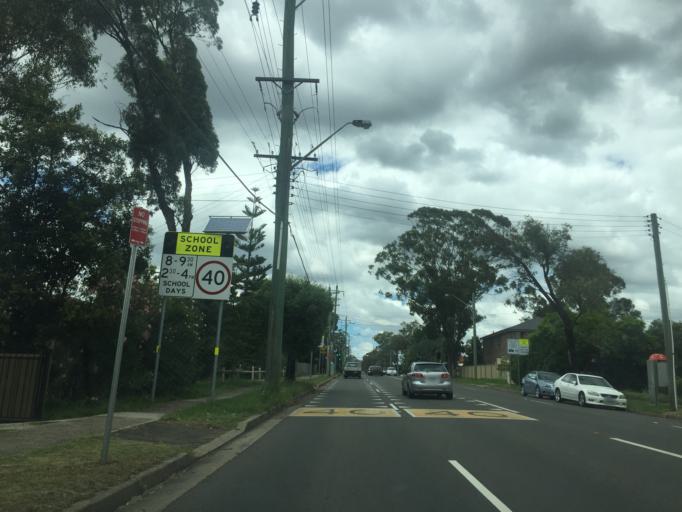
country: AU
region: New South Wales
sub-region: Blacktown
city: Blacktown
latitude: -33.7681
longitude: 150.8926
